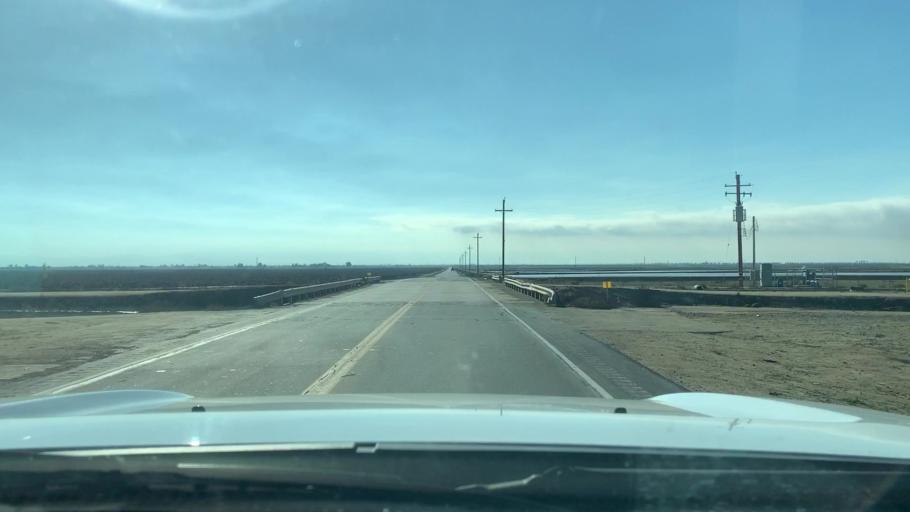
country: US
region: California
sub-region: Kern County
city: Rosedale
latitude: 35.4687
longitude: -119.1535
